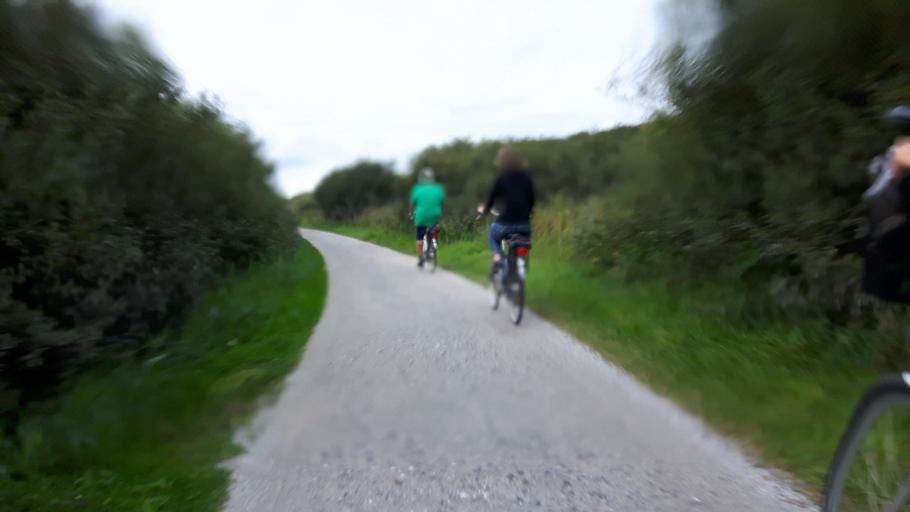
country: NL
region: Friesland
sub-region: Gemeente Ameland
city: Nes
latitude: 53.4577
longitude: 5.7487
